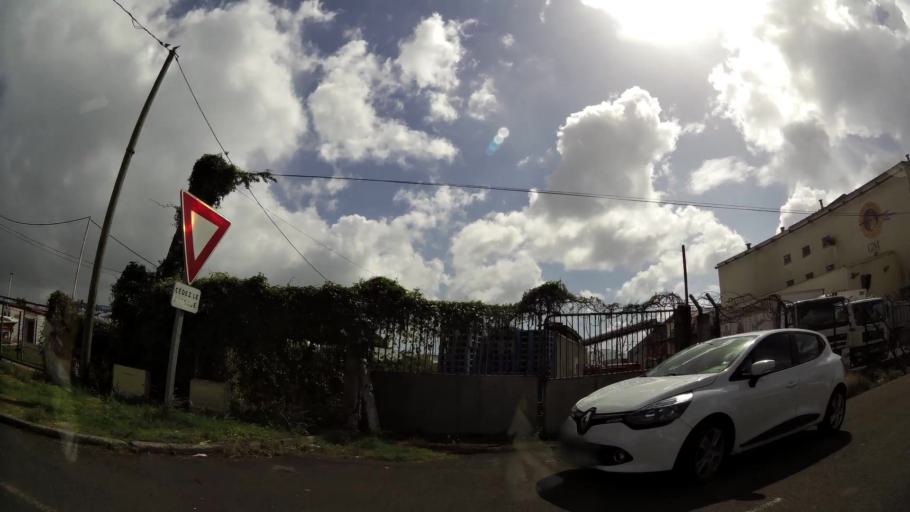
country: MQ
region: Martinique
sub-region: Martinique
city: Fort-de-France
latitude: 14.5964
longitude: -61.0555
